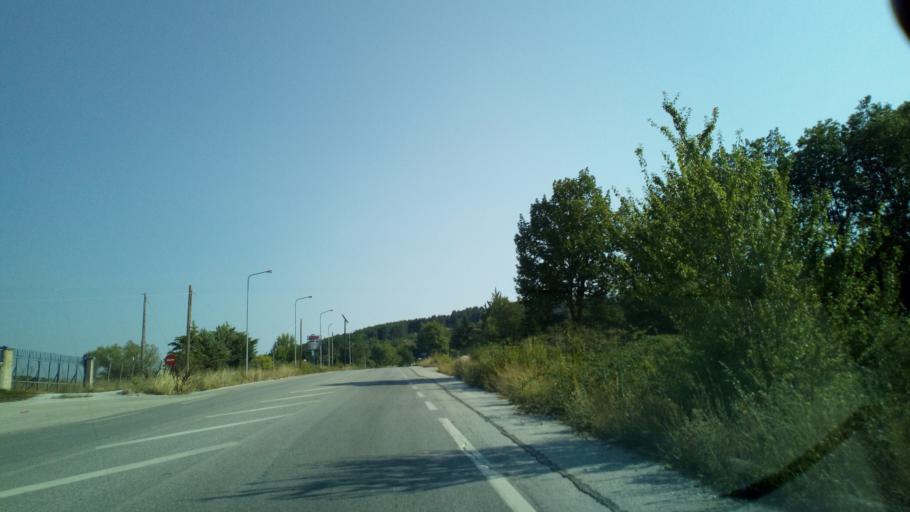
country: GR
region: Central Macedonia
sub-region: Nomos Chalkidikis
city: Polygyros
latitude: 40.4053
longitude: 23.4214
